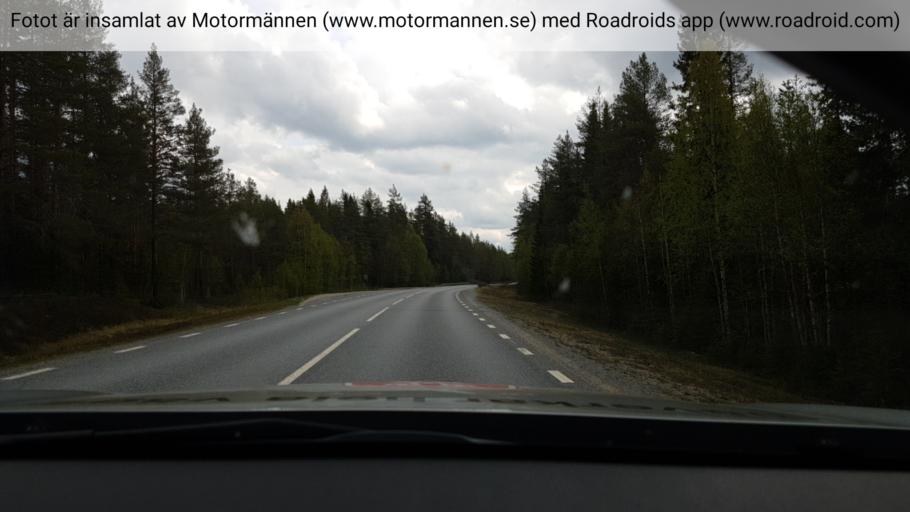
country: SE
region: Vaesterbotten
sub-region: Bjurholms Kommun
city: Bjurholm
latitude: 63.9712
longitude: 18.8316
